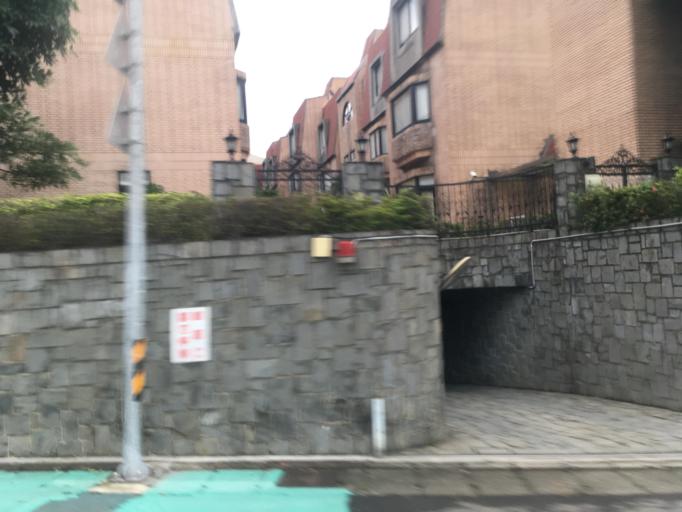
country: TW
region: Taipei
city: Taipei
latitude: 25.1313
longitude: 121.5281
